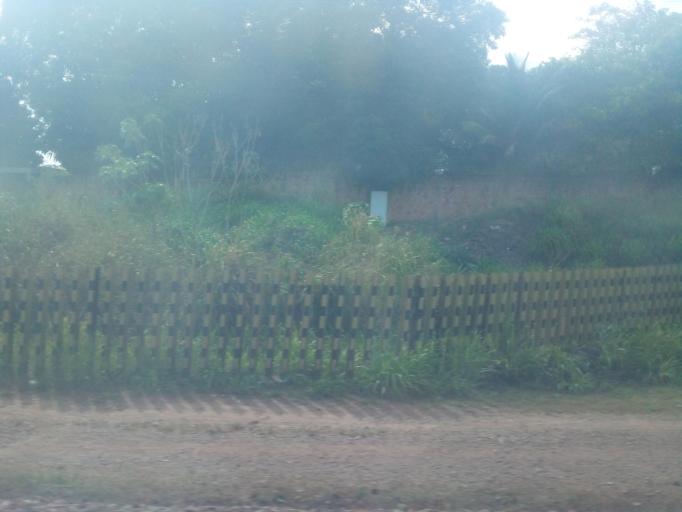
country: BR
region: Maranhao
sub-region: Sao Luis
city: Sao Luis
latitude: -2.6965
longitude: -44.3072
